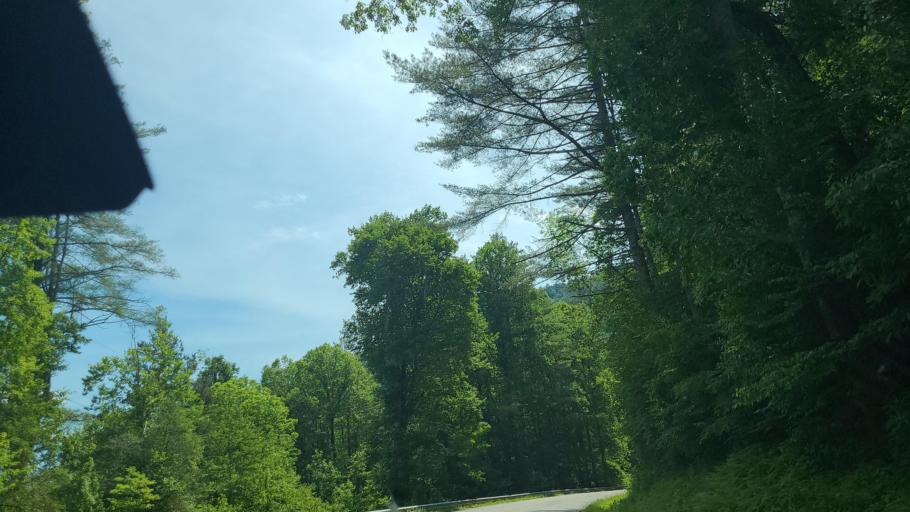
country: US
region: South Carolina
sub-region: Oconee County
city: Walhalla
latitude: 34.9097
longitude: -83.1760
